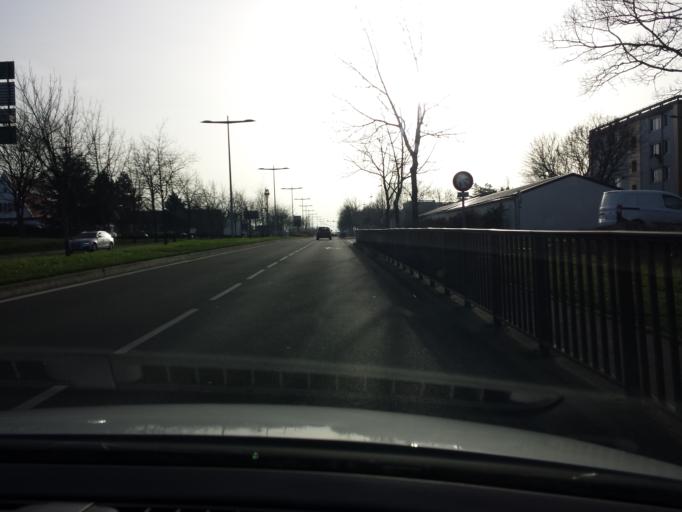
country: FR
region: Haute-Normandie
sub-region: Departement de l'Eure
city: Evreux
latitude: 49.0143
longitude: 1.1695
